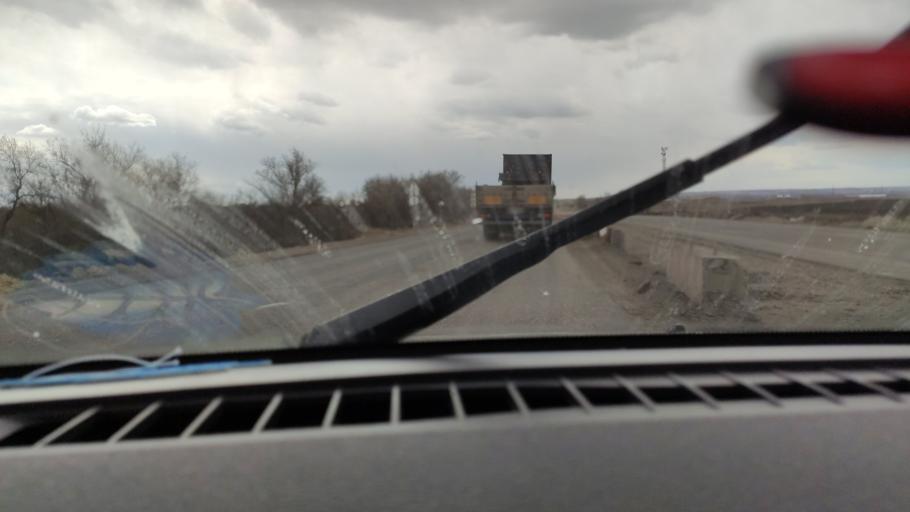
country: RU
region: Saratov
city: Sinodskoye
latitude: 52.0003
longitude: 46.6778
